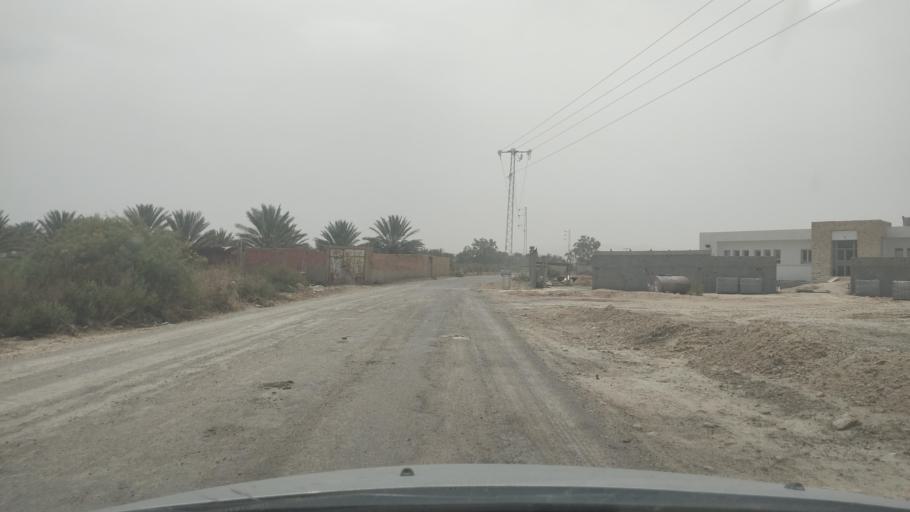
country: TN
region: Gafsa
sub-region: Gafsa Municipality
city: Gafsa
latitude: 34.3240
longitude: 8.9530
